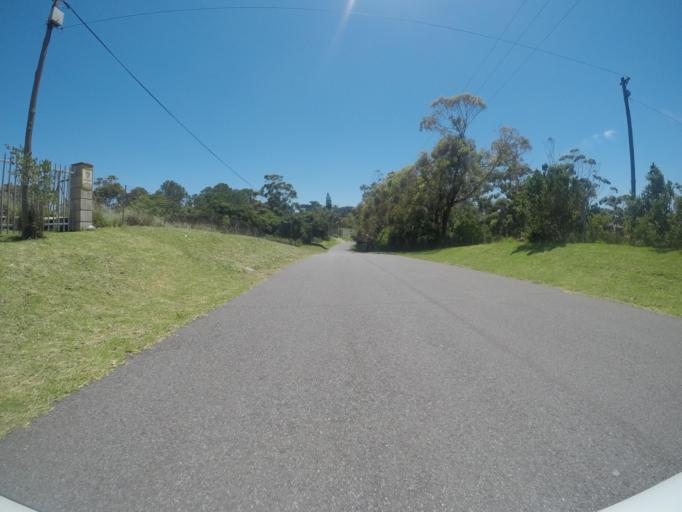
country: ZA
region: Eastern Cape
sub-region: Buffalo City Metropolitan Municipality
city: East London
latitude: -32.9359
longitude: 28.0044
